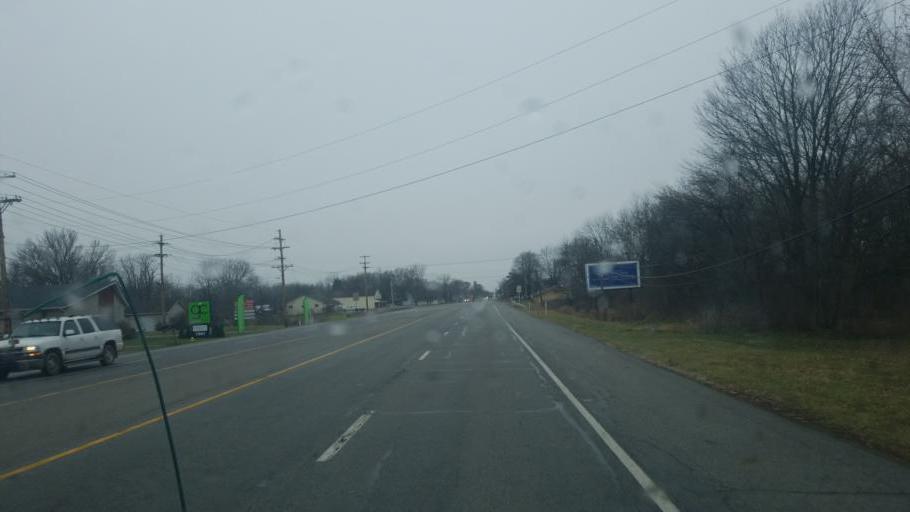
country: US
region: Indiana
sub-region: Hancock County
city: Greenfield
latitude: 39.7865
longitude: -85.7439
